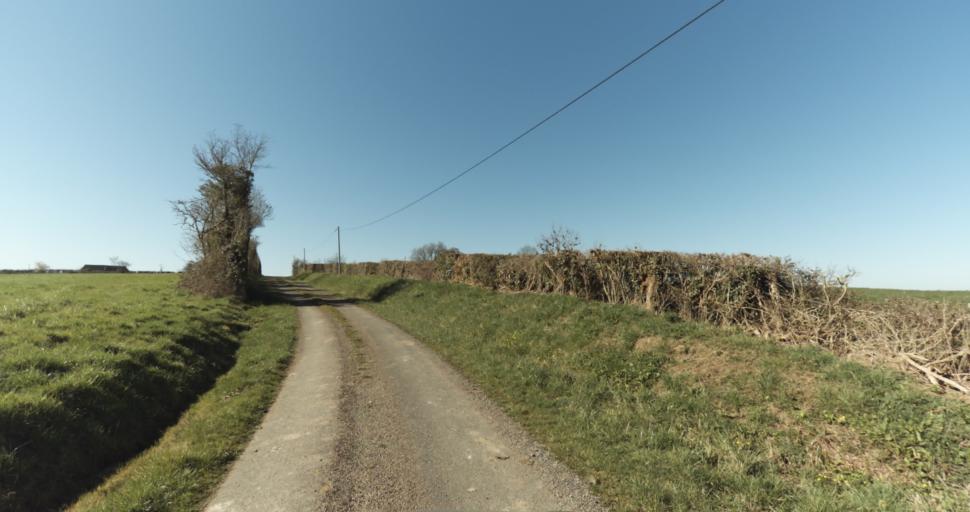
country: FR
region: Lower Normandy
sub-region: Departement de l'Orne
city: Trun
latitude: 48.9217
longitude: 0.0355
